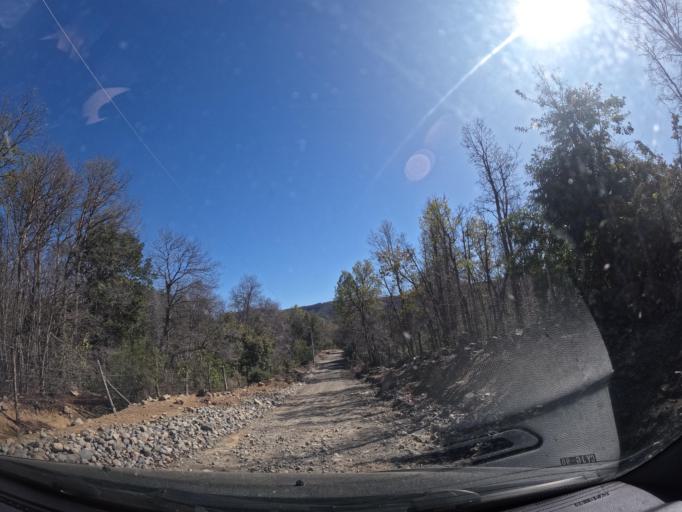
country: CL
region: Maule
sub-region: Provincia de Linares
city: Longavi
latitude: -36.2375
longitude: -71.3567
